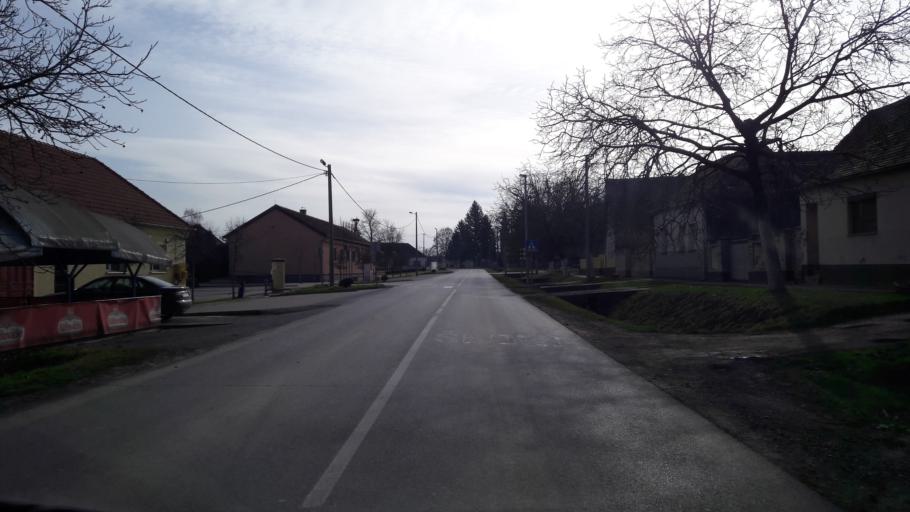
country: HR
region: Osjecko-Baranjska
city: Semeljci
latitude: 45.3538
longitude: 18.5553
